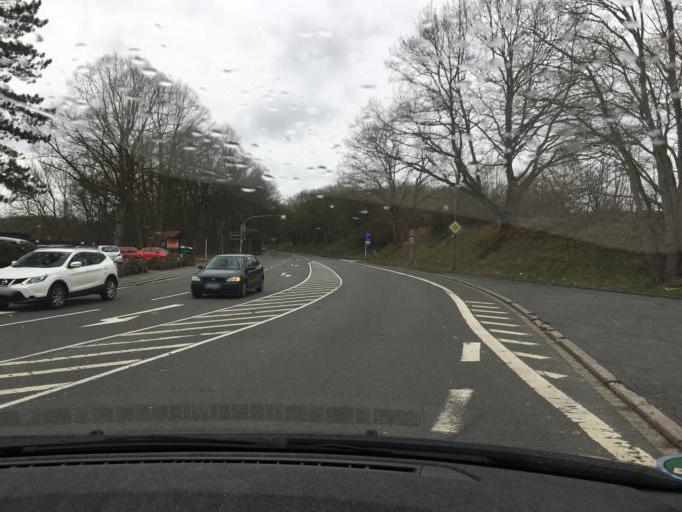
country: DE
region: North Rhine-Westphalia
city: Herdecke
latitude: 51.4257
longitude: 7.4844
